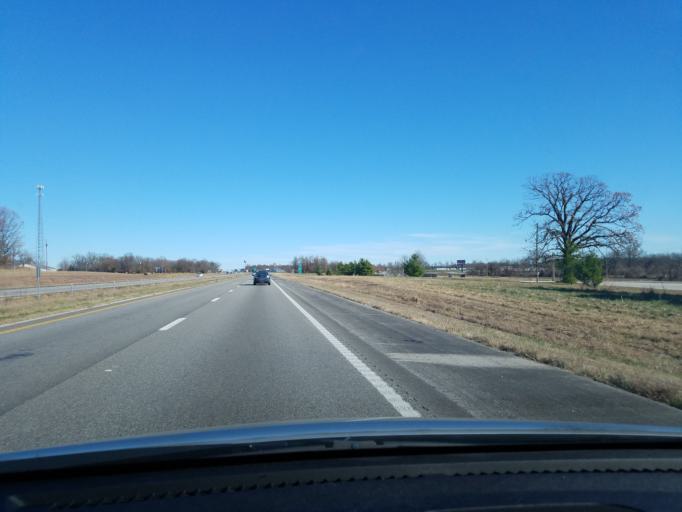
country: US
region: Missouri
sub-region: Greene County
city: Strafford
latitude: 37.2637
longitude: -93.1437
